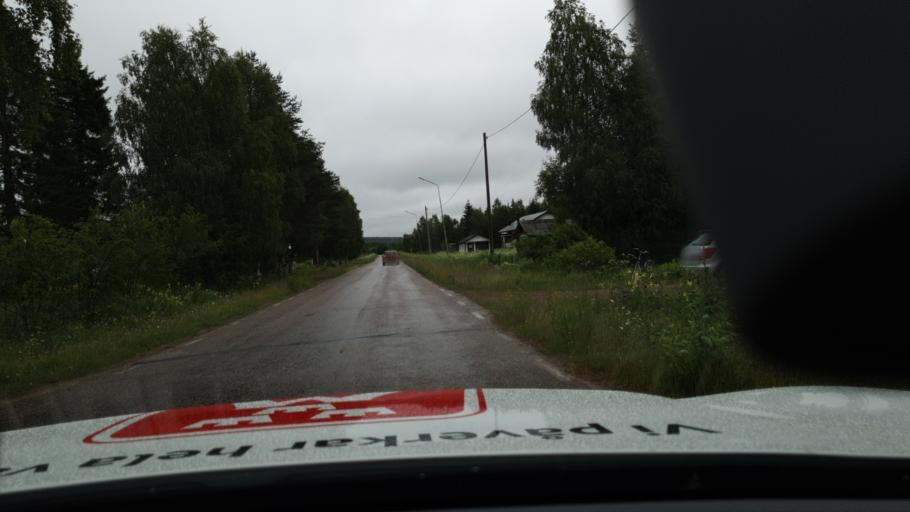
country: SE
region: Norrbotten
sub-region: Overtornea Kommun
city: OEvertornea
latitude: 66.4191
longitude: 23.6046
